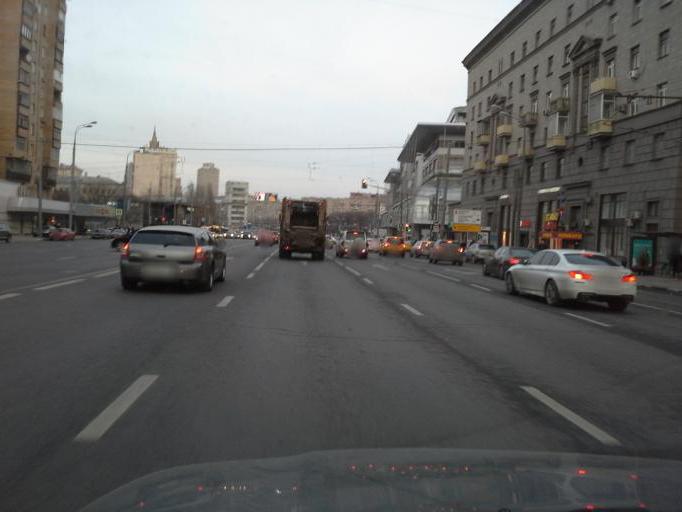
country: RU
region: Moskovskaya
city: Dorogomilovo
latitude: 55.7459
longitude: 37.5632
